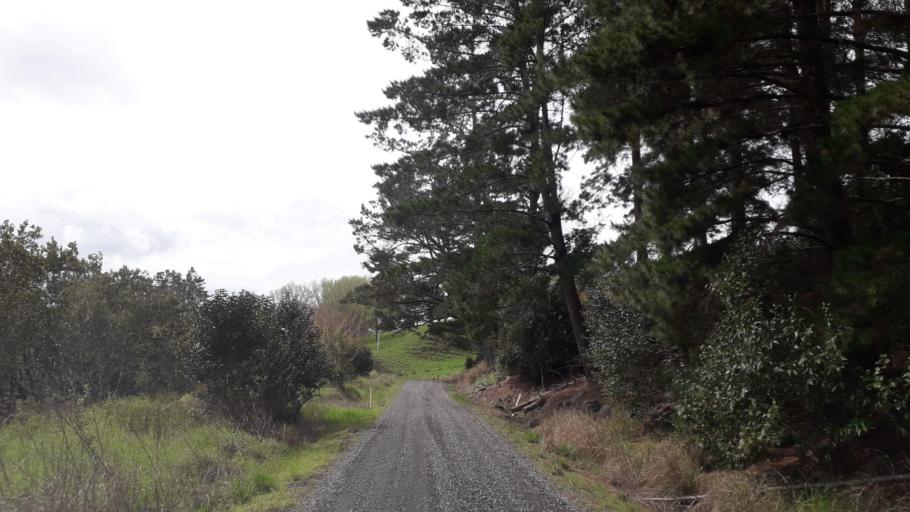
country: NZ
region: Northland
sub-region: Far North District
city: Waimate North
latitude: -35.3033
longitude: 173.5646
